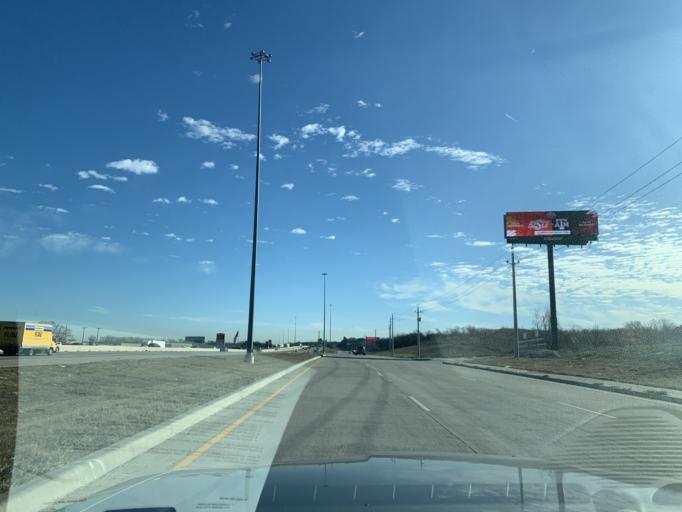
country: US
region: Texas
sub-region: Dallas County
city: Grand Prairie
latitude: 32.7589
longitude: -97.0042
